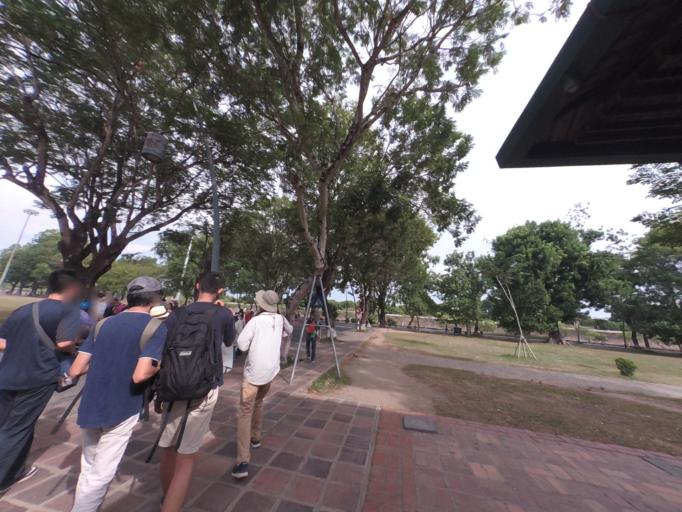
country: VN
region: Thua Thien-Hue
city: Hue
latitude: 16.4679
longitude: 107.5813
